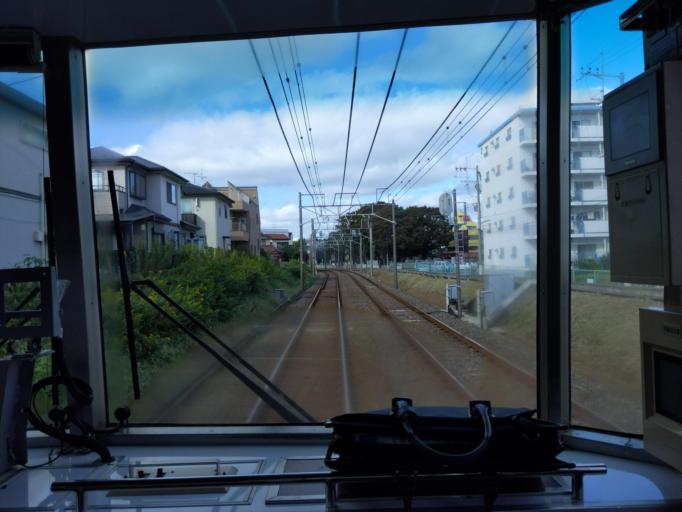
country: JP
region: Chiba
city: Funabashi
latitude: 35.7175
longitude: 140.0434
